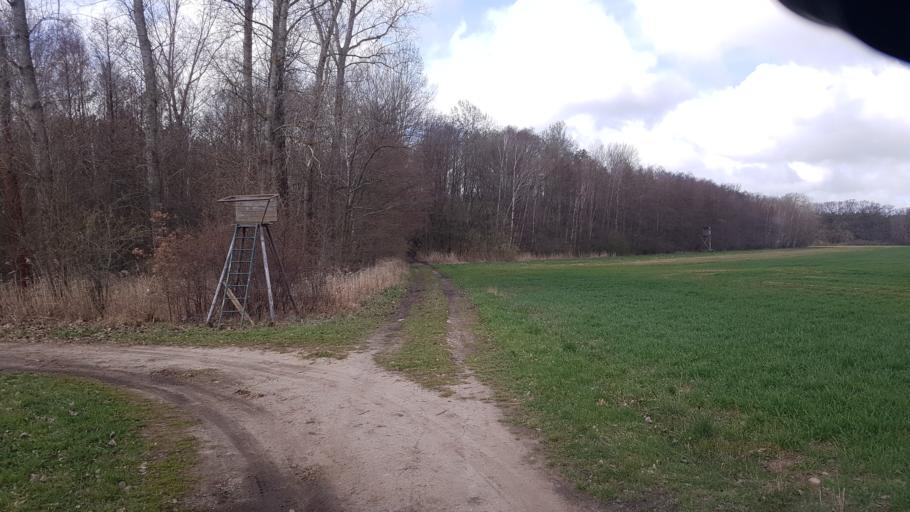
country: DE
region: Brandenburg
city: Doberlug-Kirchhain
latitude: 51.6445
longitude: 13.5256
